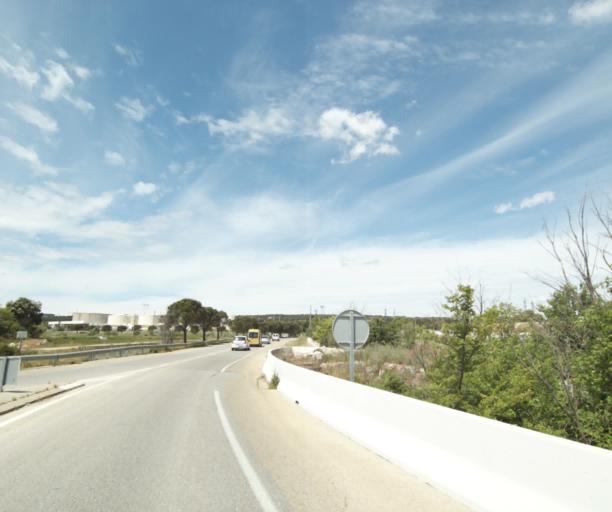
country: FR
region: Provence-Alpes-Cote d'Azur
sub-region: Departement des Bouches-du-Rhone
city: Rognac
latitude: 43.5023
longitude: 5.2232
